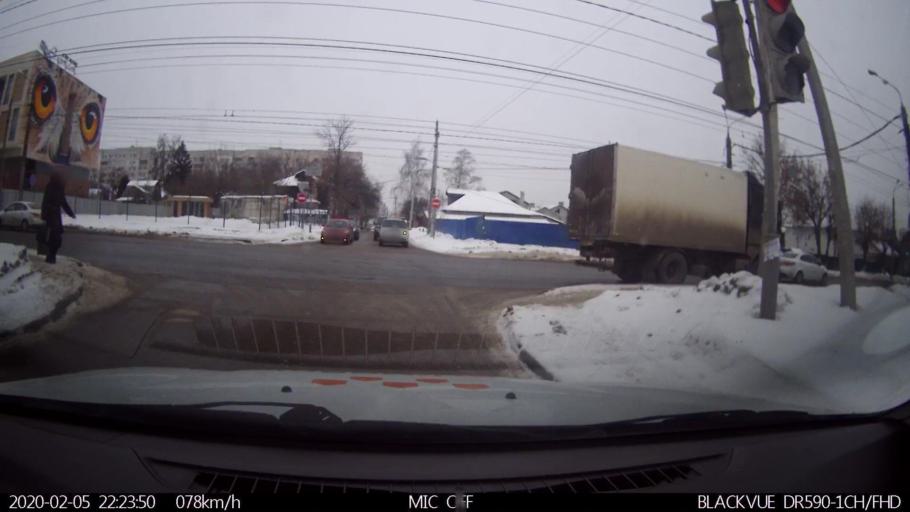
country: RU
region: Nizjnij Novgorod
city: Pervomaysk
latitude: 54.7676
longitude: 44.0430
